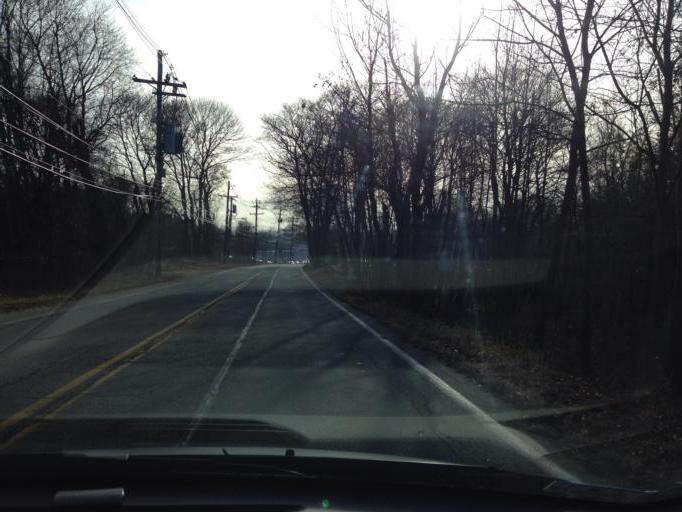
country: US
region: Massachusetts
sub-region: Middlesex County
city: Bedford
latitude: 42.4974
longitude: -71.2871
